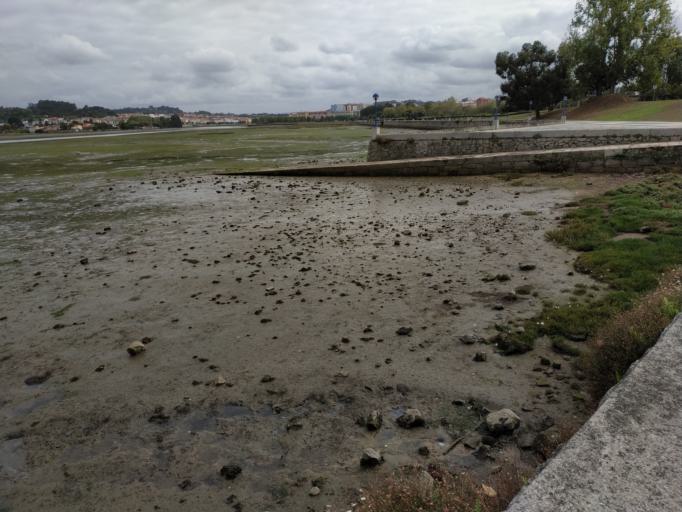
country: ES
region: Galicia
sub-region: Provincia da Coruna
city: Culleredo
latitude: 43.3257
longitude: -8.3802
